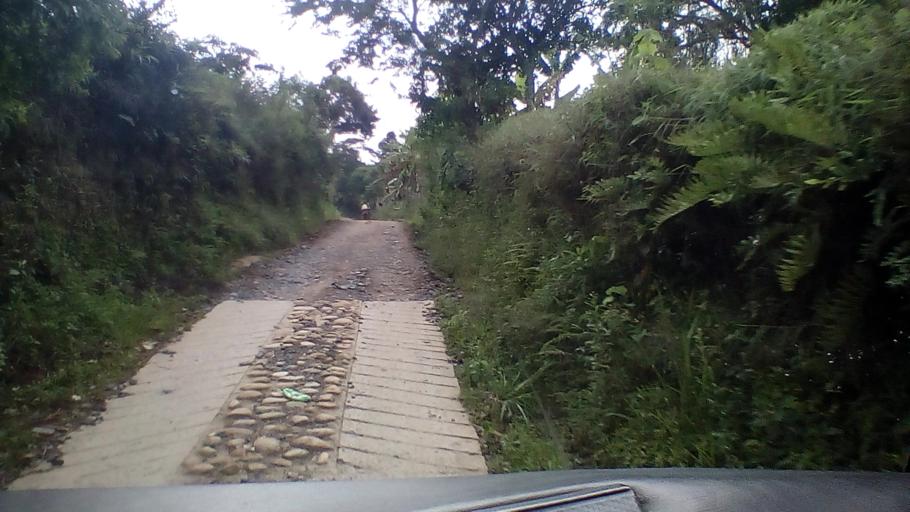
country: CO
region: Boyaca
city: Santana
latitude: 6.0031
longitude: -73.5068
